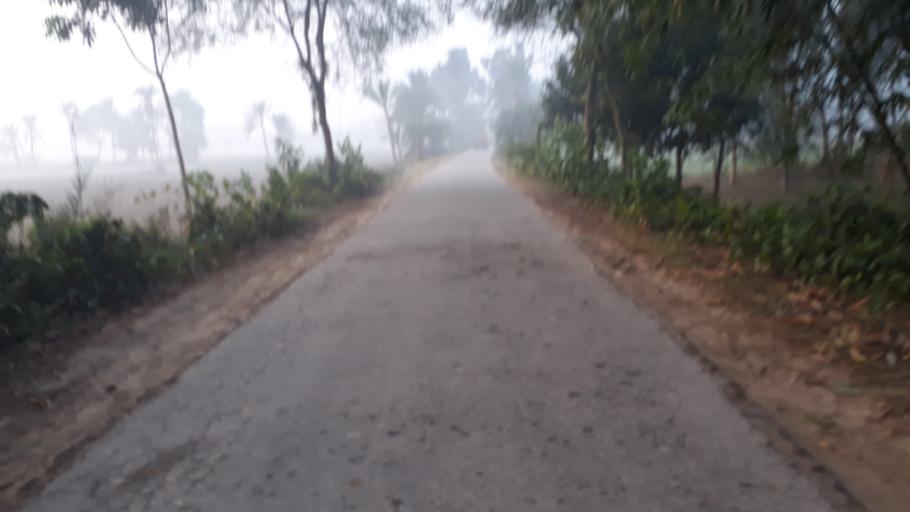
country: BD
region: Khulna
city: Jhingergacha
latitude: 23.2640
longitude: 88.9347
